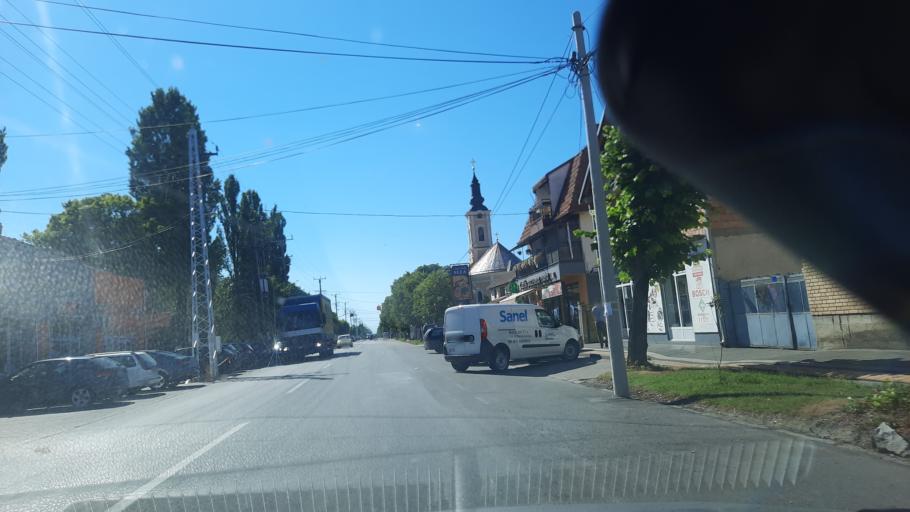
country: RS
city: Simanovci
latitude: 44.8741
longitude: 20.0921
